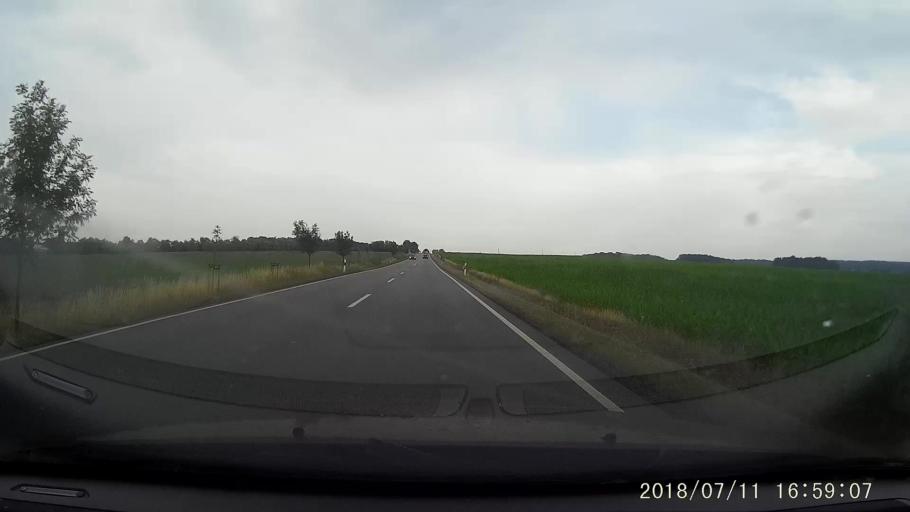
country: DE
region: Saxony
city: Niesky
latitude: 51.2694
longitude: 14.8462
